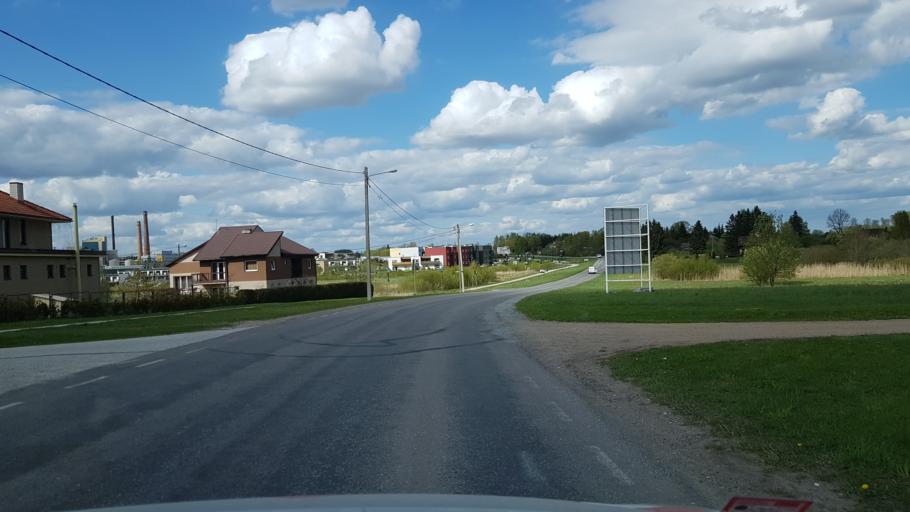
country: EE
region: Tartu
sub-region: Tartu linn
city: Tartu
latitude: 58.3611
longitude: 26.7968
